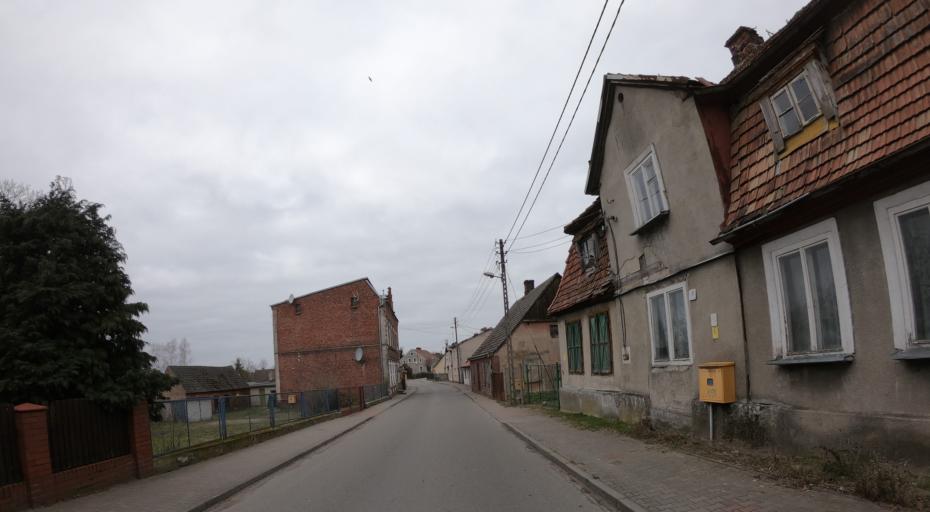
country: PL
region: West Pomeranian Voivodeship
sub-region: Powiat goleniowski
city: Stepnica
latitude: 53.6597
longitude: 14.5158
